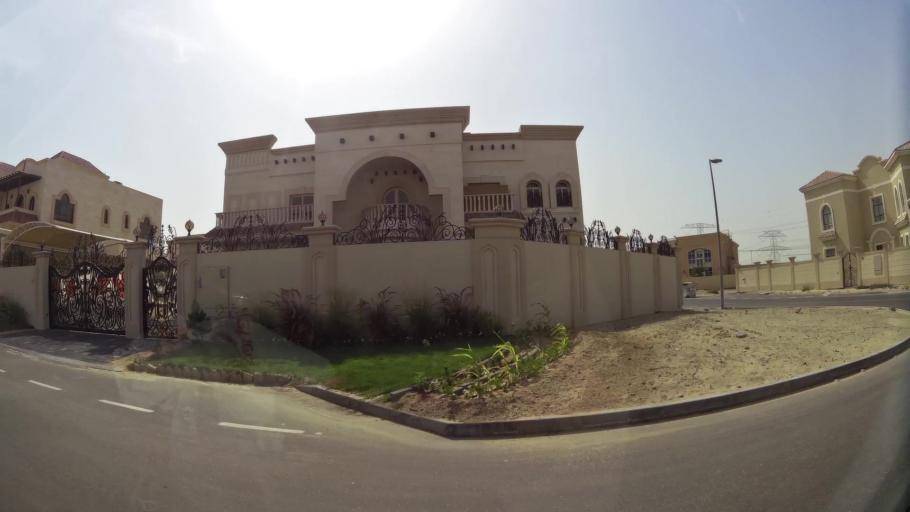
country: AE
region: Ash Shariqah
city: Sharjah
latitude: 25.2685
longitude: 55.4681
